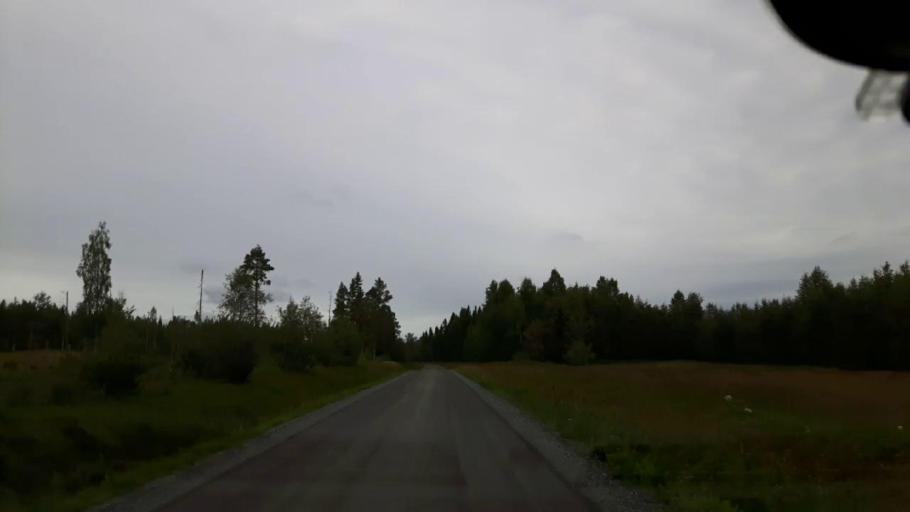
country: SE
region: Jaemtland
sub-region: Krokoms Kommun
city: Krokom
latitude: 63.2843
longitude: 14.3850
